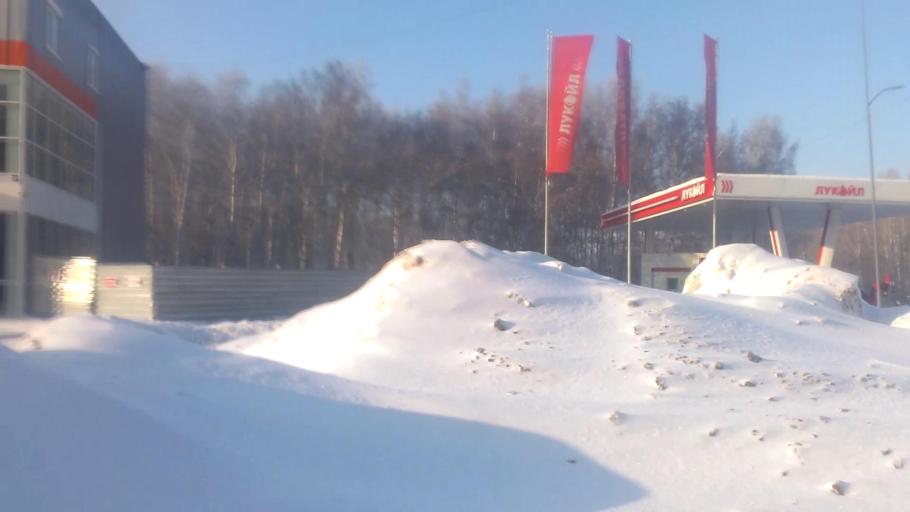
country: RU
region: Altai Krai
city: Novosilikatnyy
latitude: 53.3747
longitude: 83.6632
